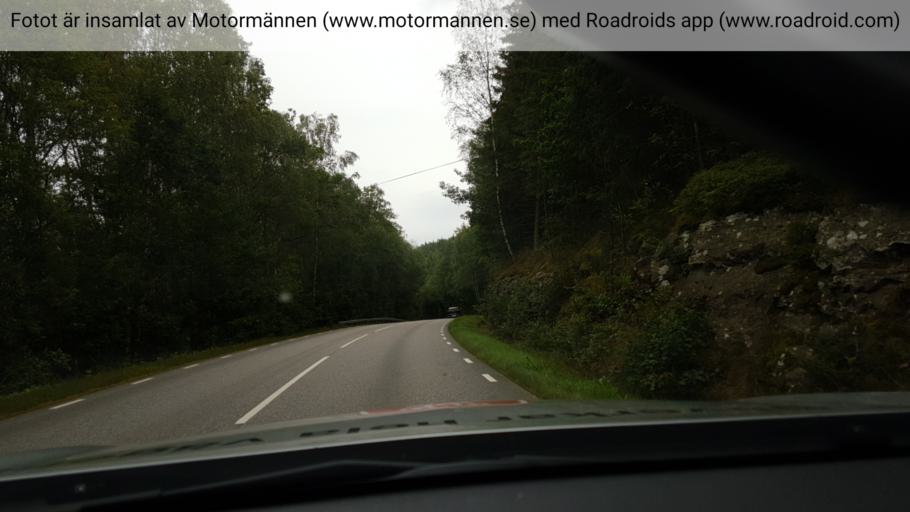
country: SE
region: Vaestra Goetaland
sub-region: Harryda Kommun
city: Hindas
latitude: 57.6144
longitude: 12.3969
